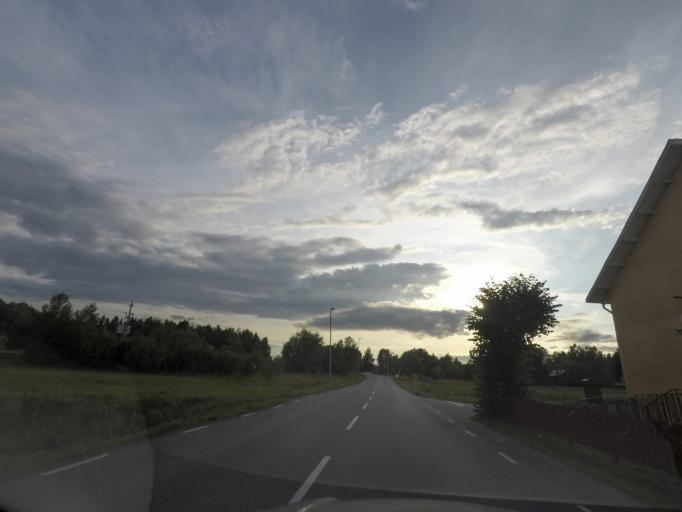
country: SE
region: OErebro
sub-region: Lindesbergs Kommun
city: Frovi
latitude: 59.4545
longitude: 15.4561
